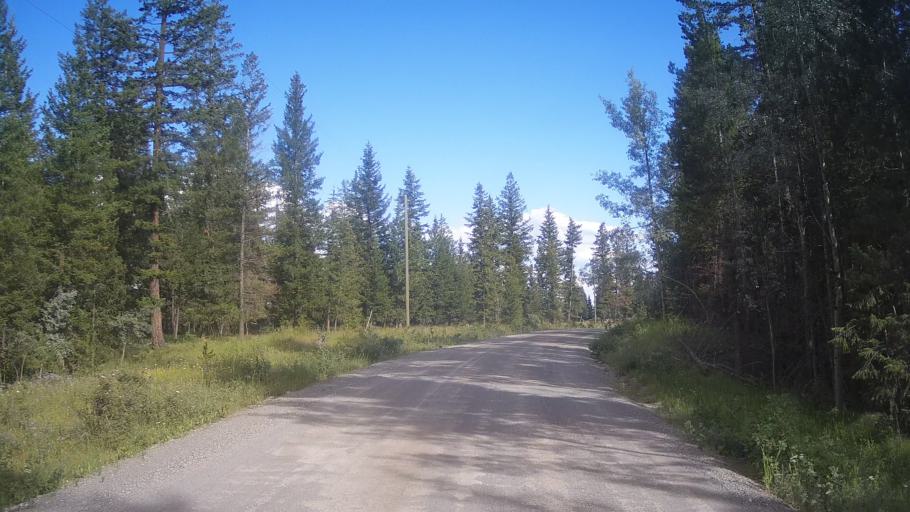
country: CA
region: British Columbia
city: Cache Creek
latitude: 51.1919
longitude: -121.5876
